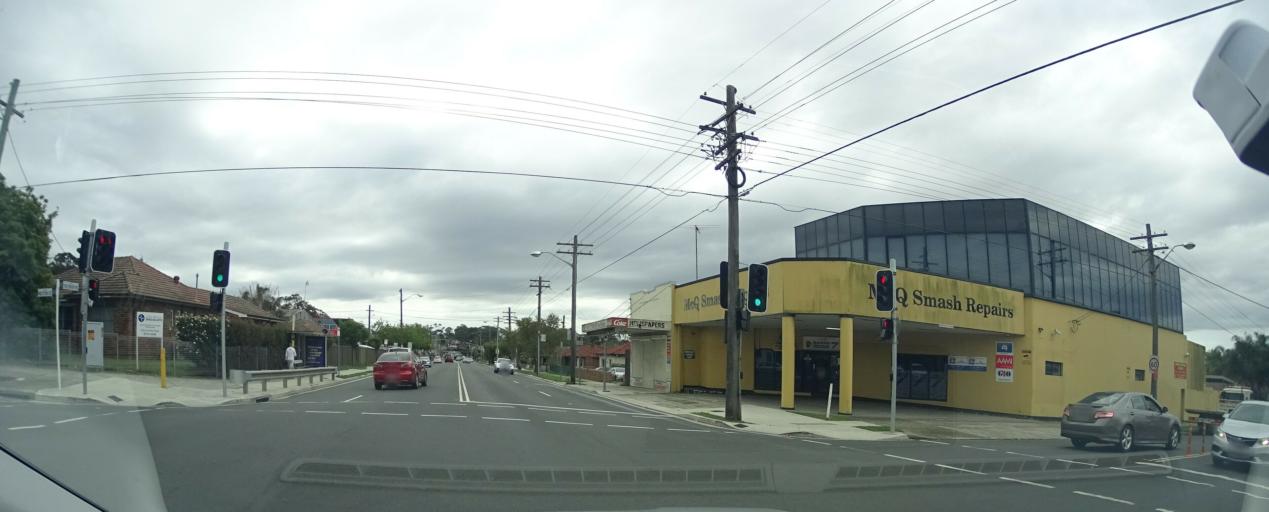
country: AU
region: New South Wales
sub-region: Bankstown
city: Revesby
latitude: -33.9556
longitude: 151.0171
